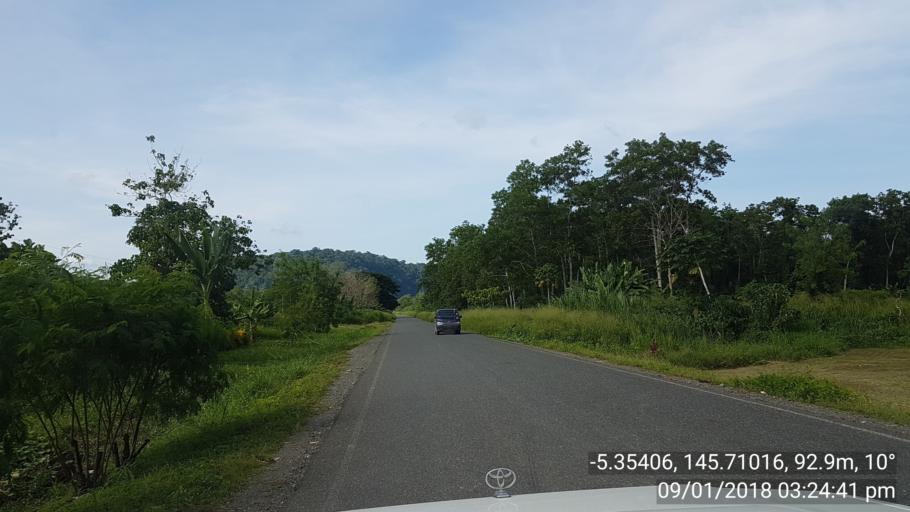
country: PG
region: Madang
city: Madang
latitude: -5.3542
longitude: 145.7103
